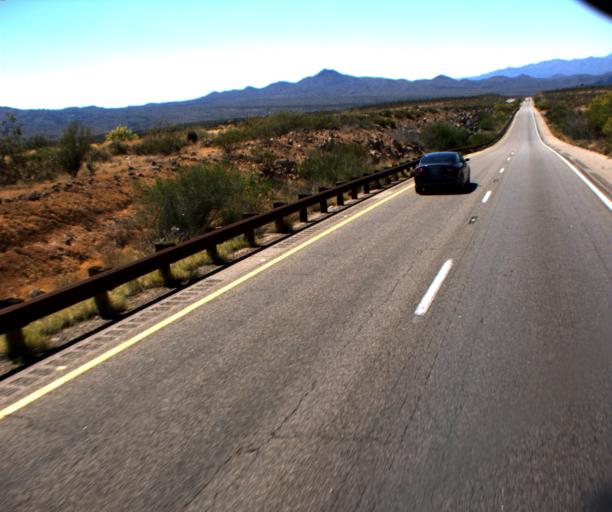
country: US
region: Arizona
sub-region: Yavapai County
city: Bagdad
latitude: 34.4868
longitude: -113.3739
